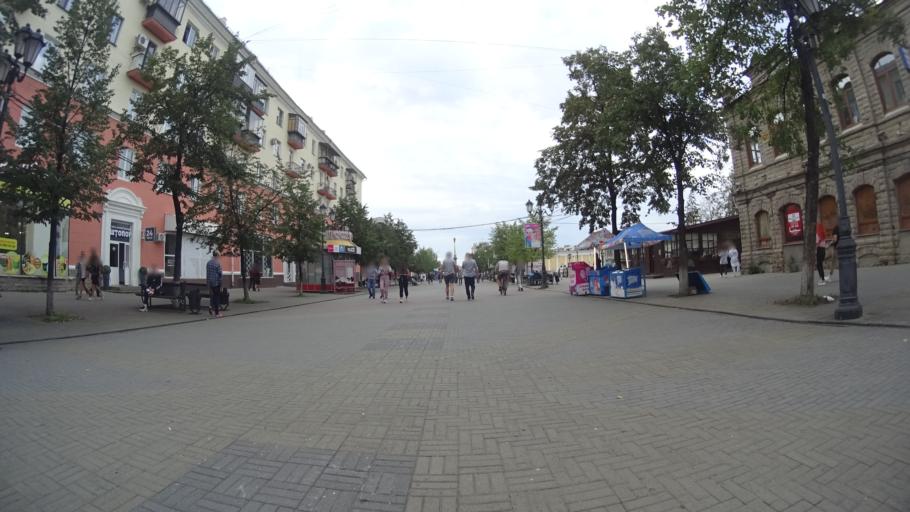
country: RU
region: Chelyabinsk
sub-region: Gorod Chelyabinsk
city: Chelyabinsk
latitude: 55.1663
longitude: 61.4005
